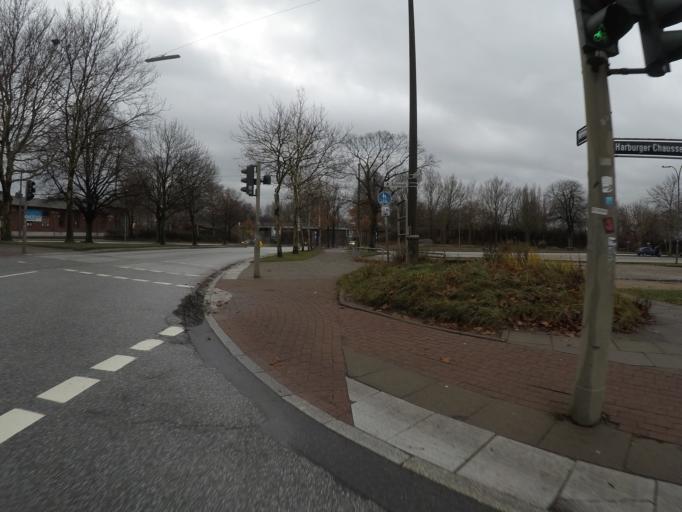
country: DE
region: Hamburg
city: Kleiner Grasbrook
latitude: 53.5209
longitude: 10.0151
